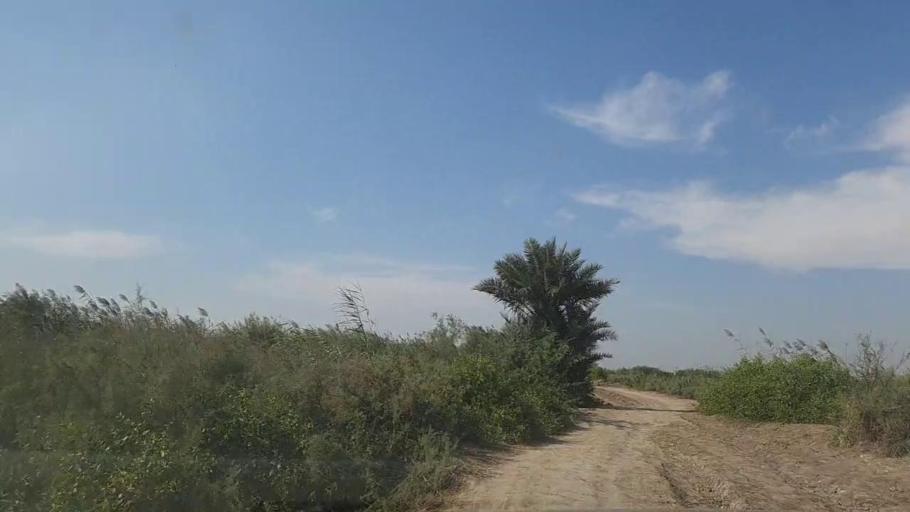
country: PK
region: Sindh
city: Mirpur Batoro
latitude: 24.8012
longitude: 68.2694
